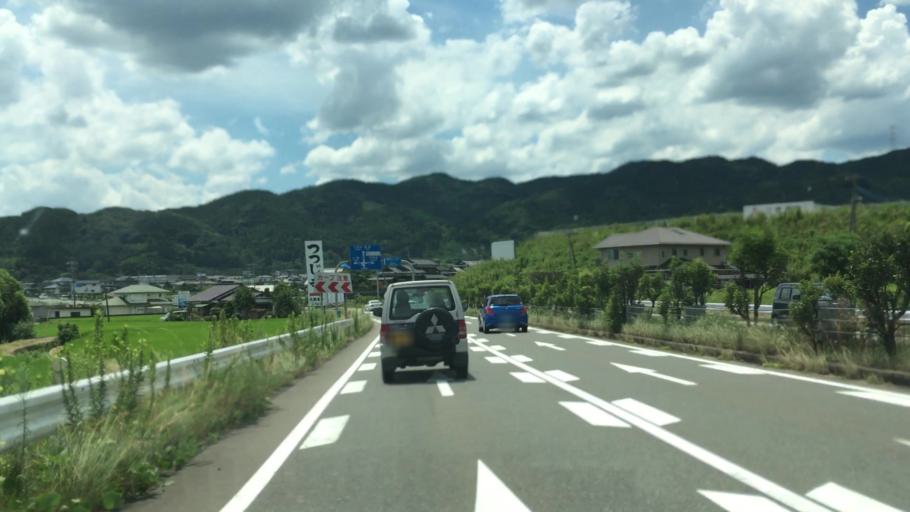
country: JP
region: Saga Prefecture
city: Tosu
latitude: 33.4228
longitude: 130.5129
